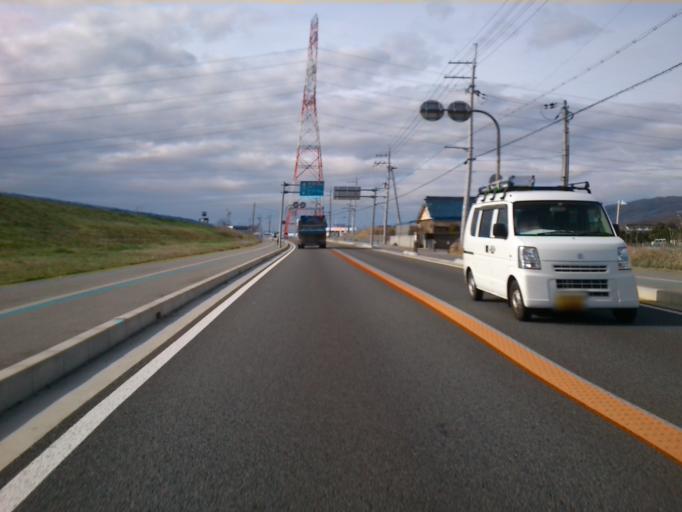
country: JP
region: Nara
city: Nara-shi
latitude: 34.7597
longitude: 135.8117
